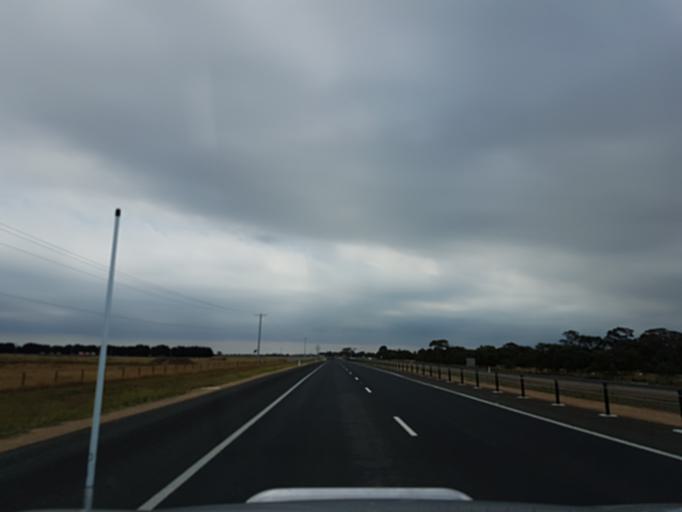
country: AU
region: Victoria
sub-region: Wellington
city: Sale
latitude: -38.1024
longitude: 147.0127
